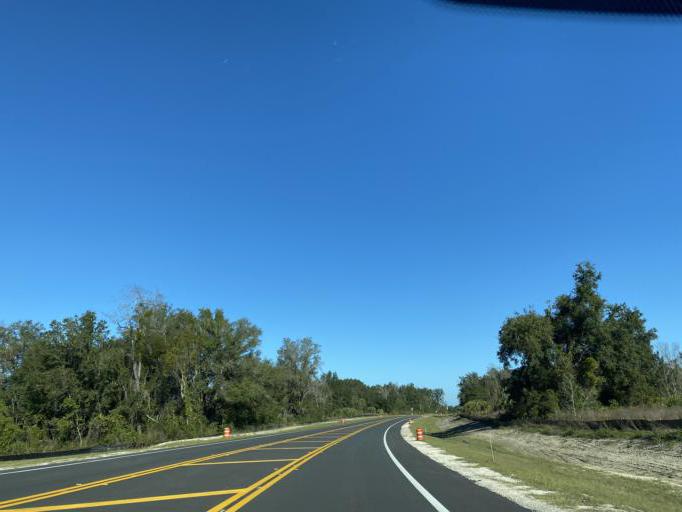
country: US
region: Florida
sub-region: Lake County
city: Mount Plymouth
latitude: 28.8173
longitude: -81.5221
